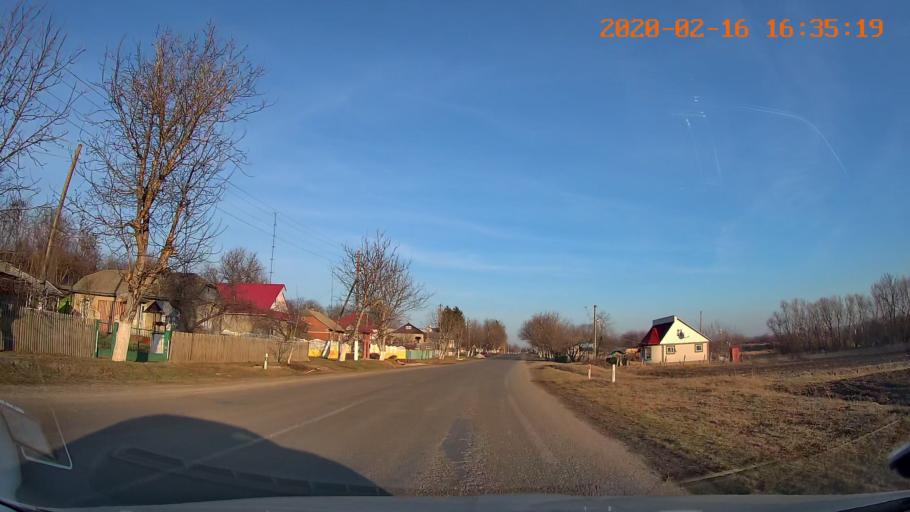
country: RO
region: Botosani
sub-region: Comuna Paltinis
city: Paltinis
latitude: 48.2706
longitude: 26.6795
